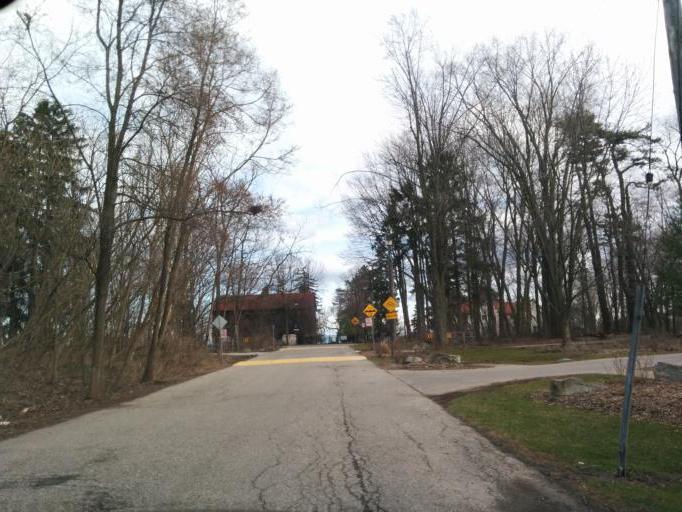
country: CA
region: Ontario
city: Mississauga
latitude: 43.5633
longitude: -79.5690
